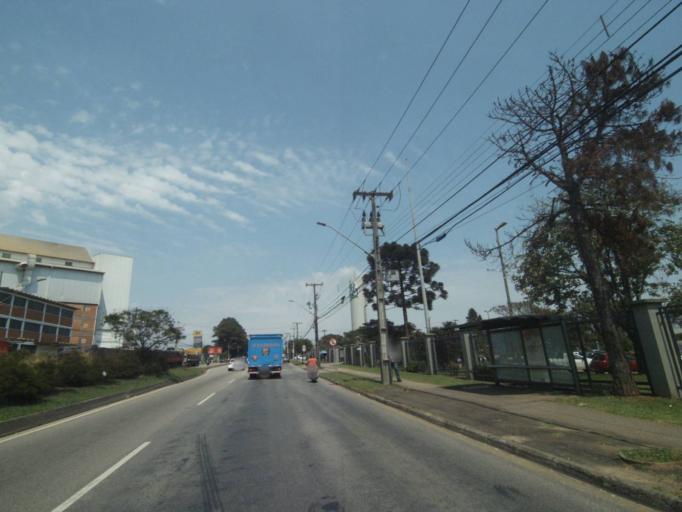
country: BR
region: Parana
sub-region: Curitiba
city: Curitiba
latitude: -25.4860
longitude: -49.3186
